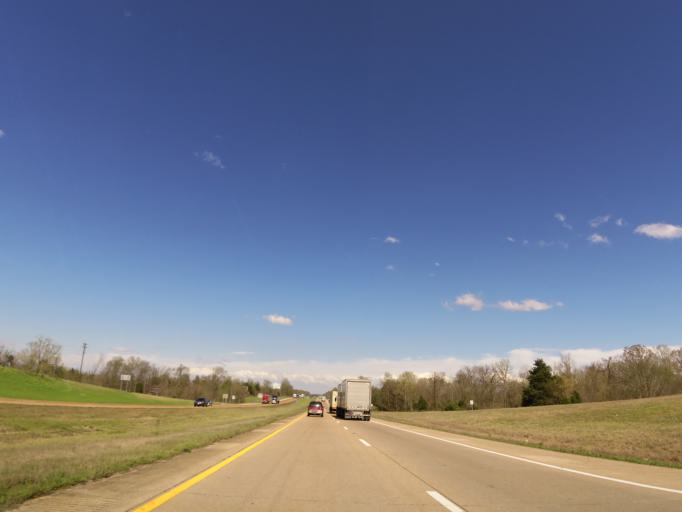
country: US
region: Tennessee
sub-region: Gibson County
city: Medina
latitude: 35.7182
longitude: -88.6335
